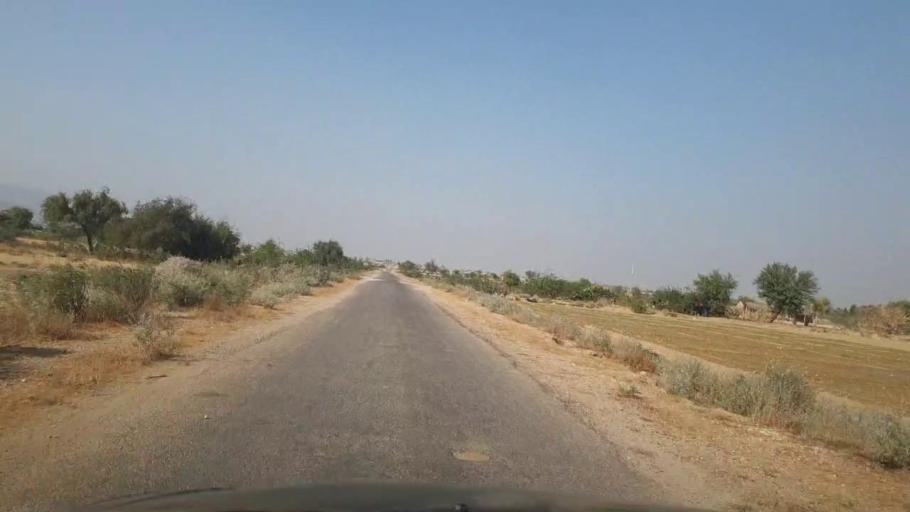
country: PK
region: Sindh
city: Jamshoro
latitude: 25.5916
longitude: 67.8185
